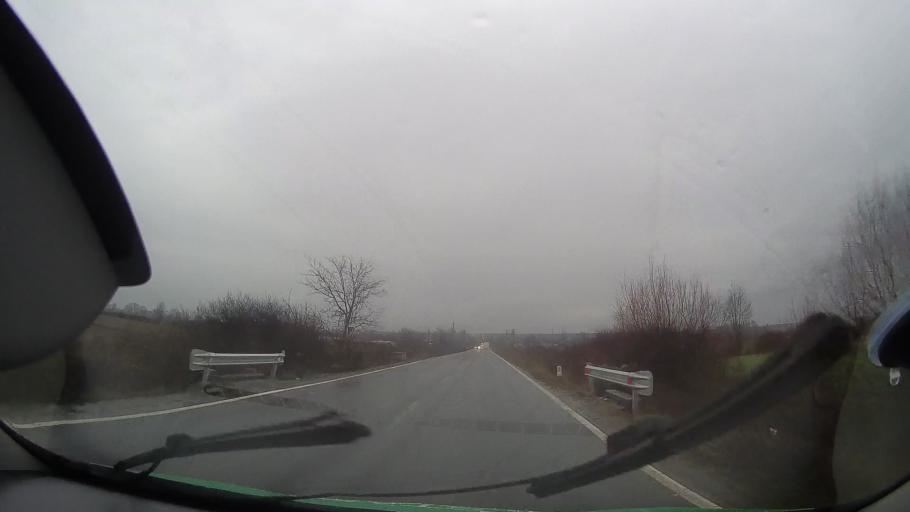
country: RO
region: Bihor
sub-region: Comuna Tinca
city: Tinca
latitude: 46.7614
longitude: 21.9347
